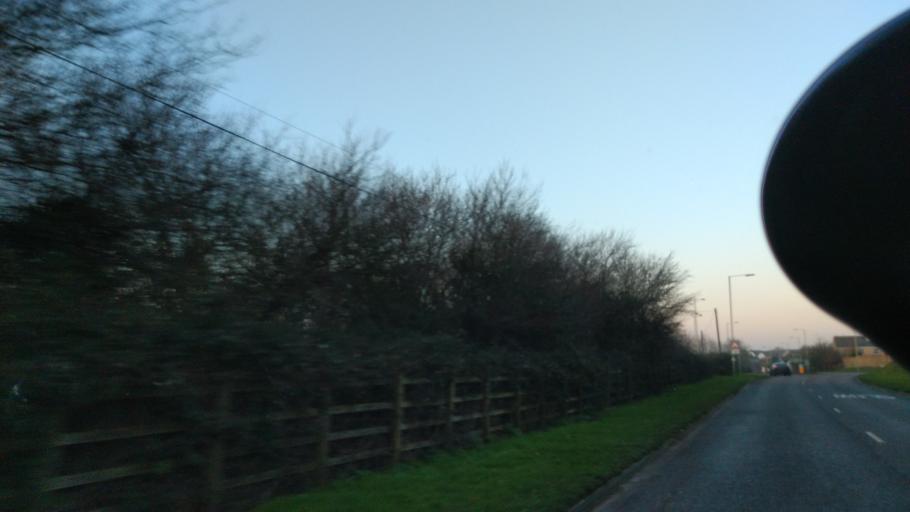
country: GB
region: England
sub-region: Wiltshire
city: Chippenham
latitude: 51.4490
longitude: -2.1130
